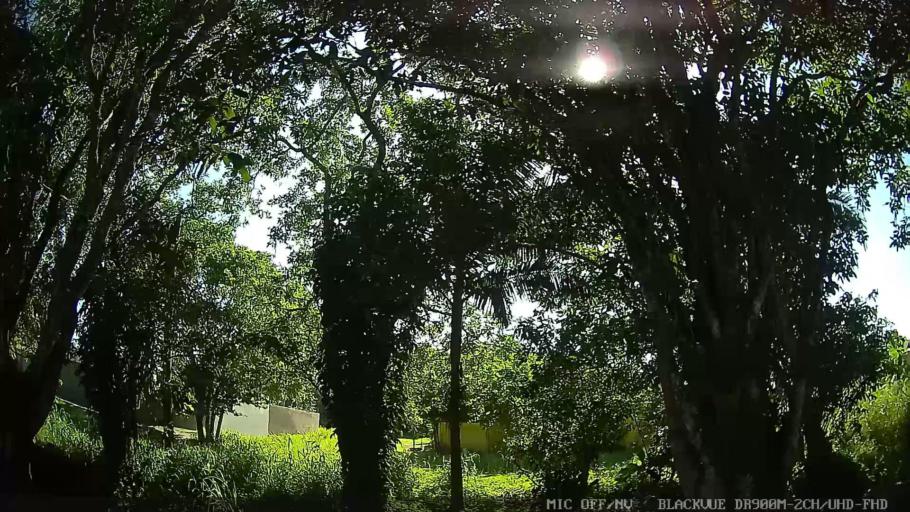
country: BR
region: Sao Paulo
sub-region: Peruibe
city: Peruibe
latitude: -24.2729
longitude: -46.9436
